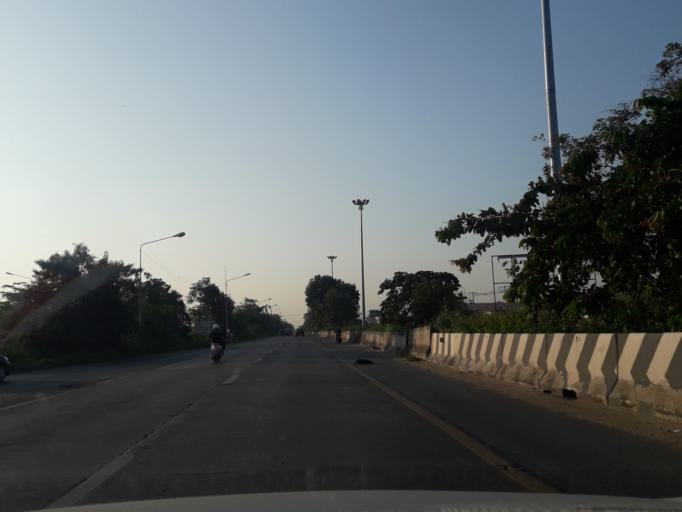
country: TH
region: Phra Nakhon Si Ayutthaya
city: Bang Pa-in
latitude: 14.1885
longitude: 100.5549
